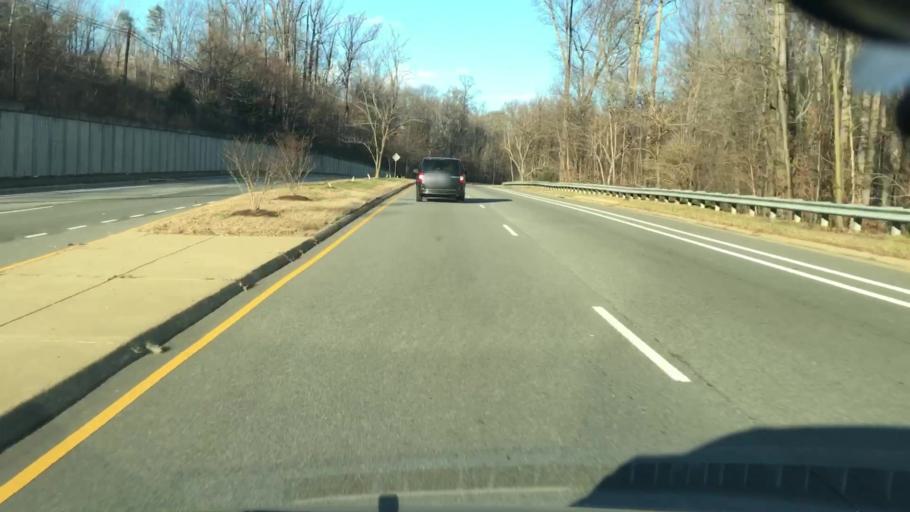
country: US
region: Virginia
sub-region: Fairfax County
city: Newington
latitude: 38.7364
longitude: -77.1686
